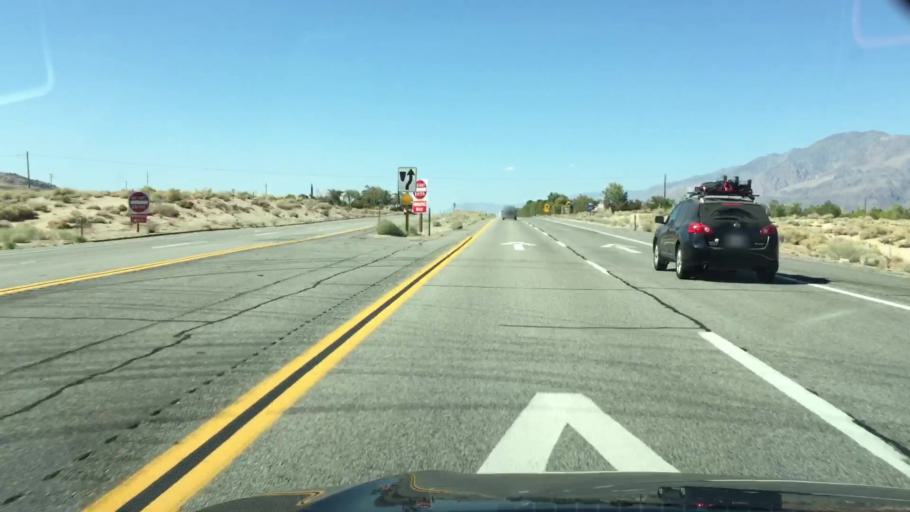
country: US
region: California
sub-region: Inyo County
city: Lone Pine
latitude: 36.5393
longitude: -118.0467
